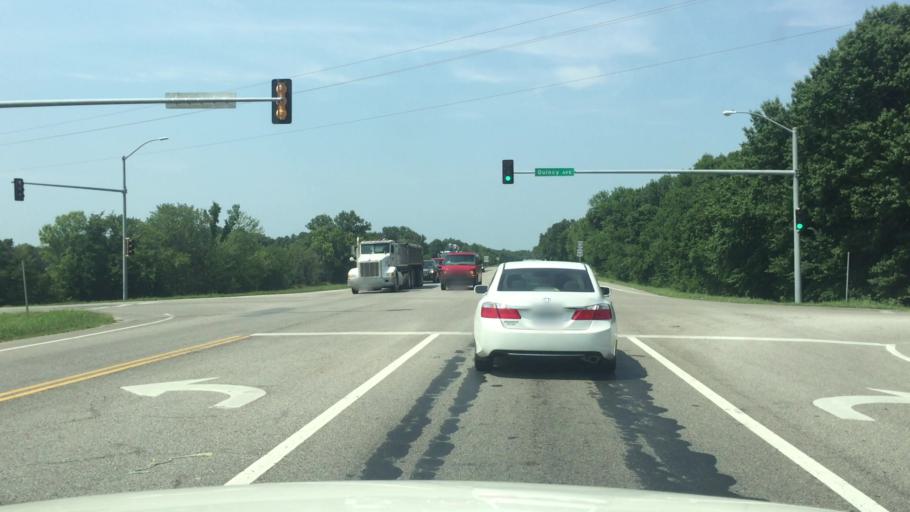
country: US
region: Kansas
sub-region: Crawford County
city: Pittsburg
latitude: 37.3964
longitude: -94.7190
